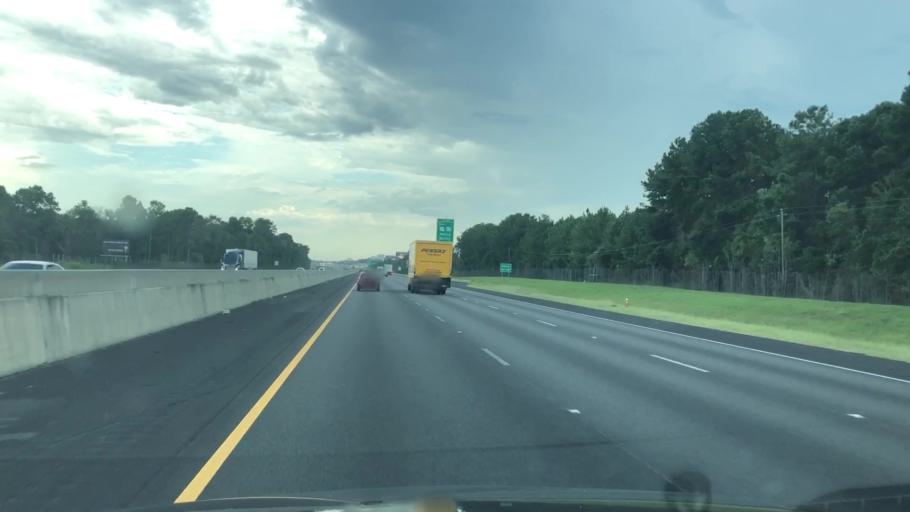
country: US
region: Georgia
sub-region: Lowndes County
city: Hahira
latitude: 31.0095
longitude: -83.3936
